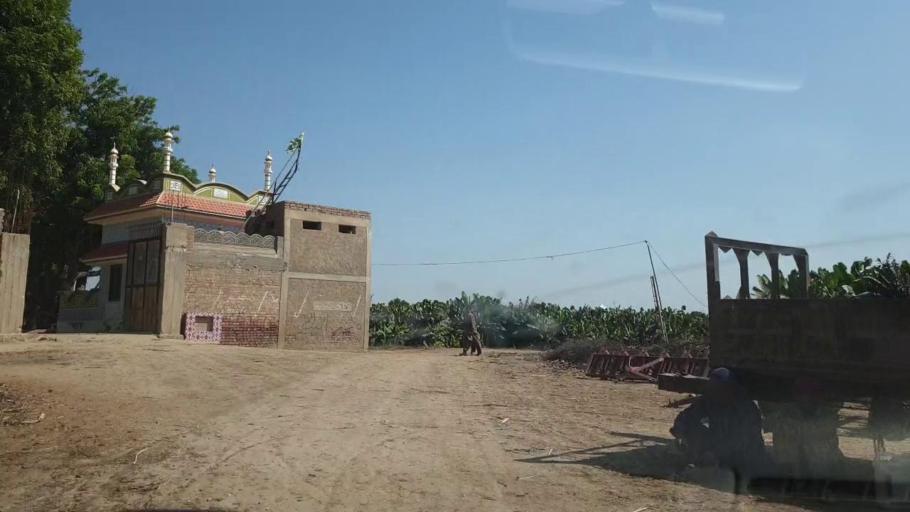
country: PK
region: Sindh
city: Tando Jam
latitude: 25.3776
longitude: 68.5797
